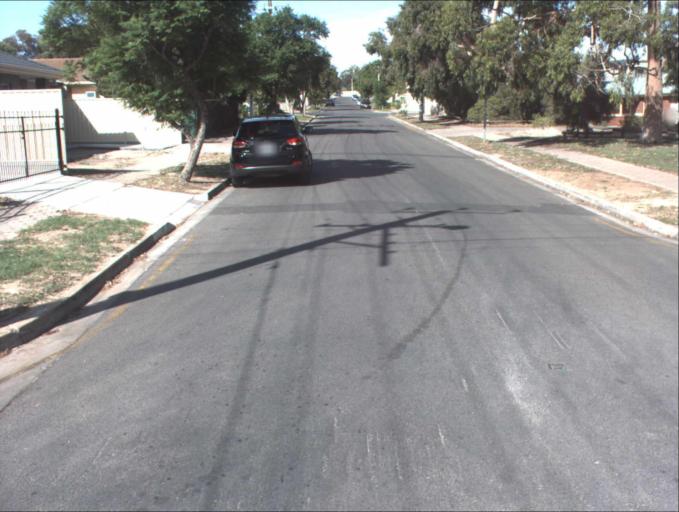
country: AU
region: South Australia
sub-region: Port Adelaide Enfield
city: Klemzig
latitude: -34.8728
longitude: 138.6406
